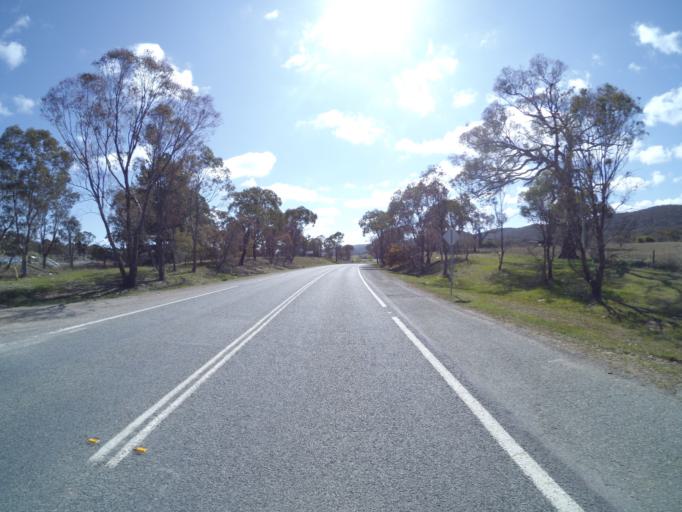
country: AU
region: New South Wales
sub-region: Queanbeyan
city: Queanbeyan
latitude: -35.3232
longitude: 149.2405
